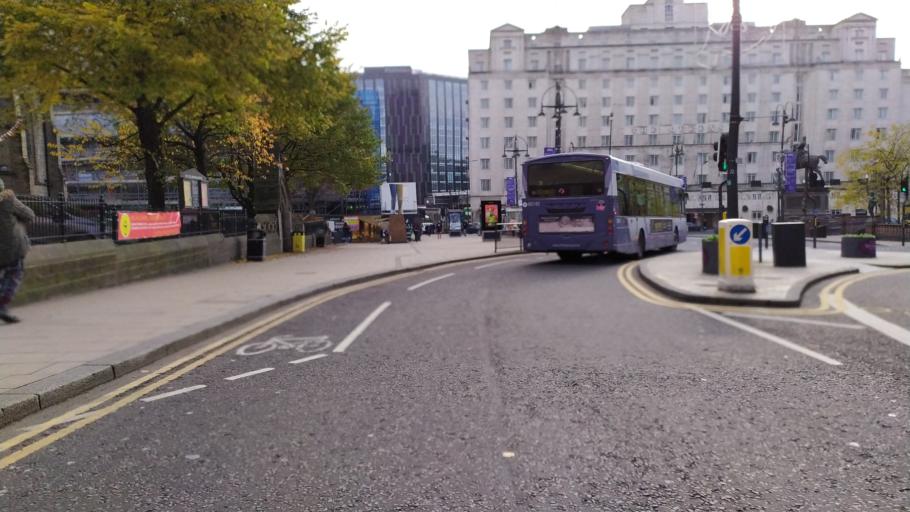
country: GB
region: England
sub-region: City and Borough of Leeds
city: Leeds
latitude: 53.7971
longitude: -1.5470
